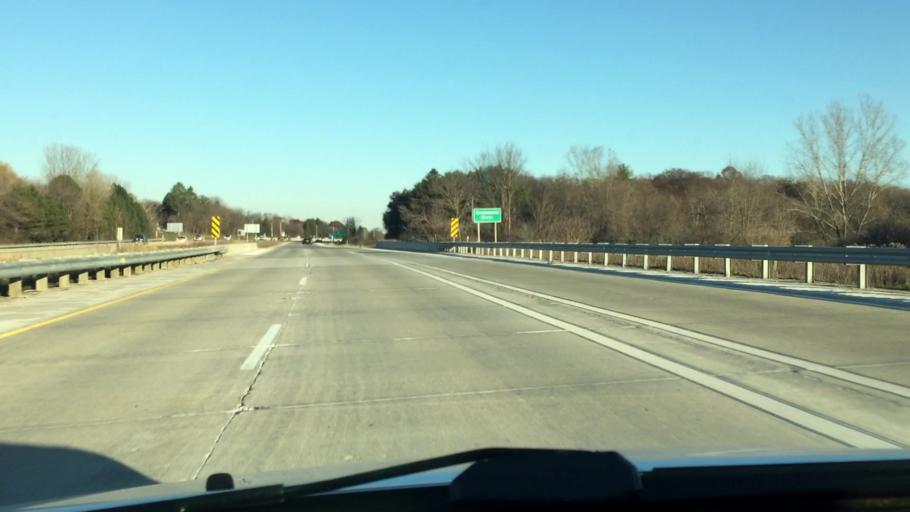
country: US
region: Wisconsin
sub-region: Waukesha County
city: Okauchee Lake
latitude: 43.1079
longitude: -88.4544
